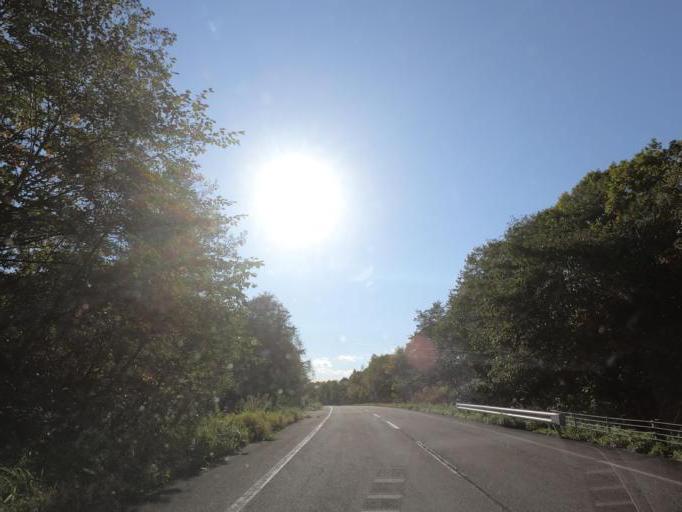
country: JP
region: Hokkaido
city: Obihiro
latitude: 42.6348
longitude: 143.4827
